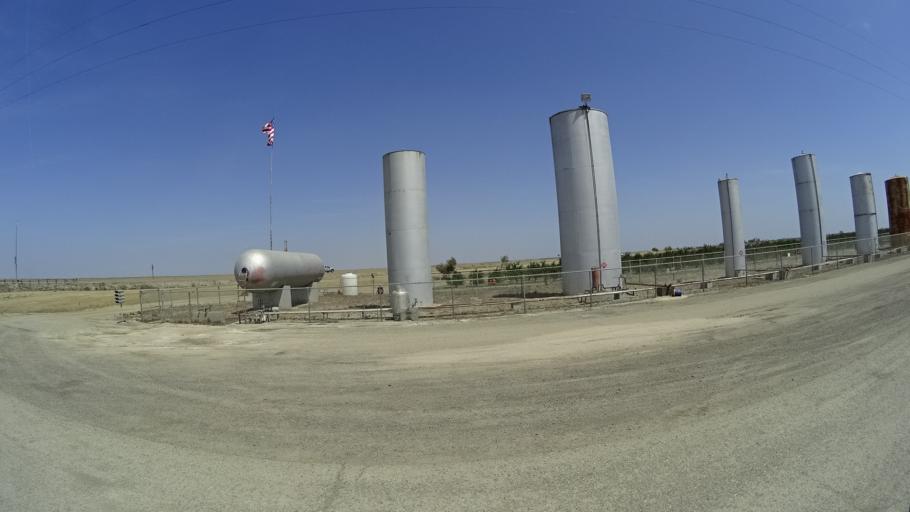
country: US
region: California
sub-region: Kings County
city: Stratford
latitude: 36.1233
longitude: -119.8906
